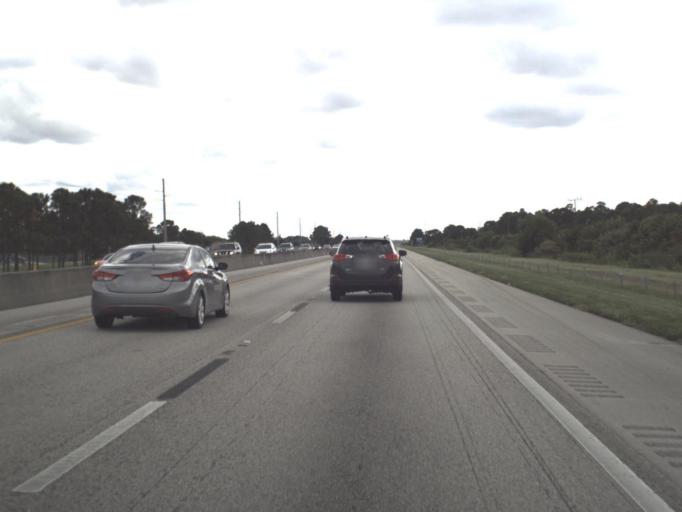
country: US
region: Florida
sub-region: Saint Lucie County
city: River Park
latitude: 27.3371
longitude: -80.3744
